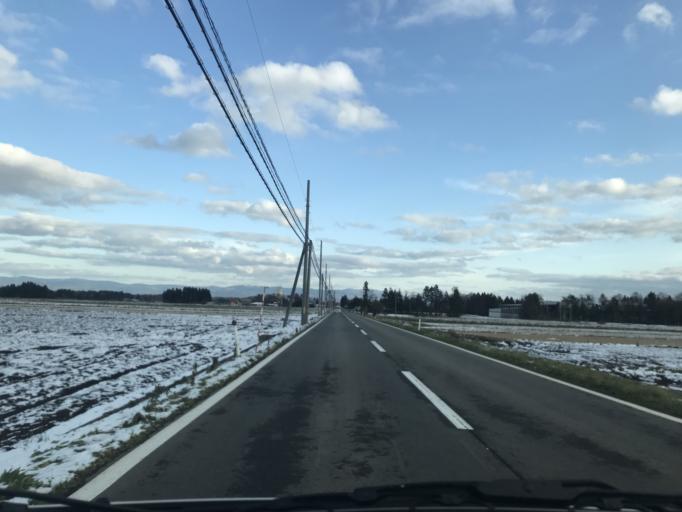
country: JP
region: Iwate
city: Kitakami
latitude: 39.2085
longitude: 141.0395
